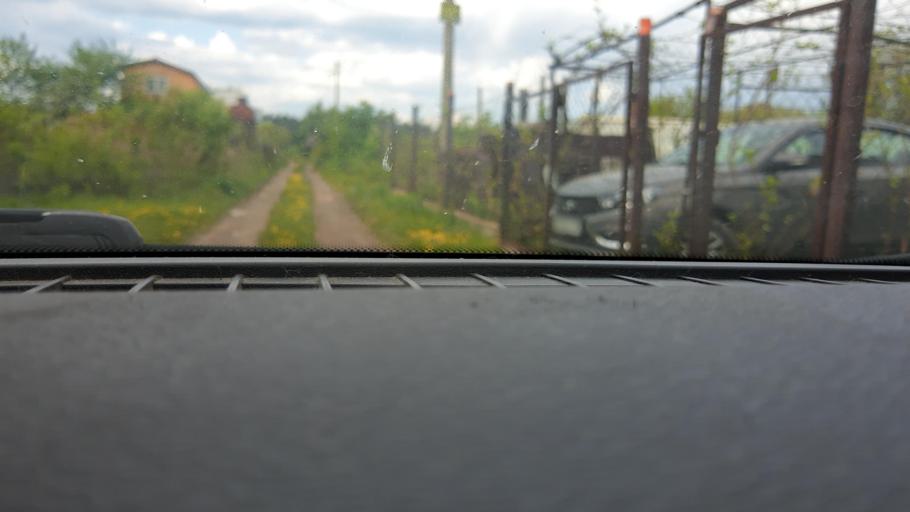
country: RU
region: Bashkortostan
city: Avdon
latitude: 54.5659
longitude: 55.7442
